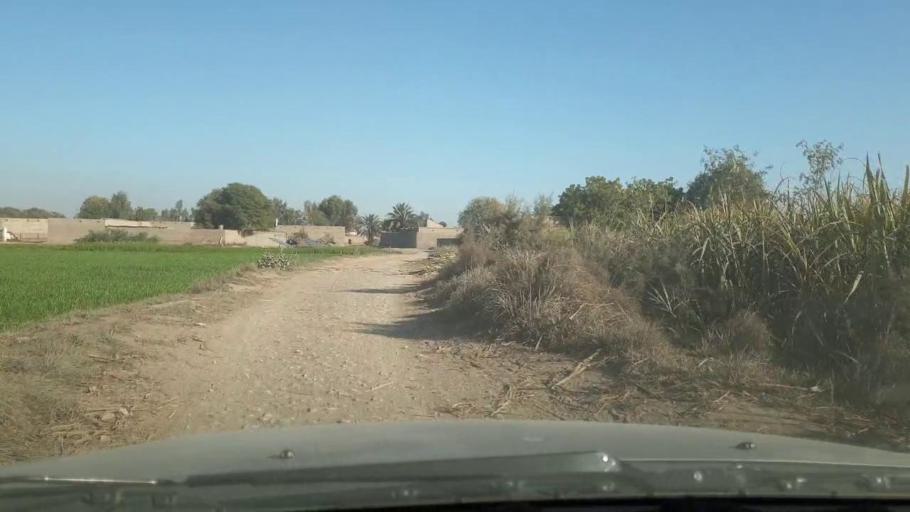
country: PK
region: Sindh
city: Adilpur
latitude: 27.9606
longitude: 69.2061
